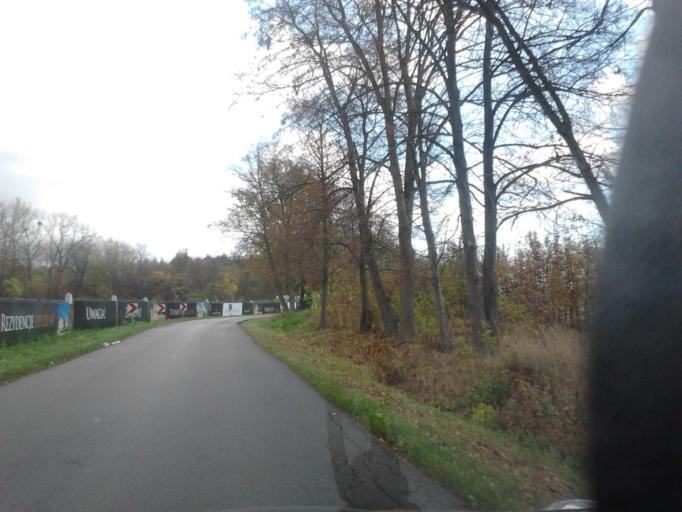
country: PL
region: Masovian Voivodeship
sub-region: Powiat pruszkowski
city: Nadarzyn
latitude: 52.0926
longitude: 20.8424
